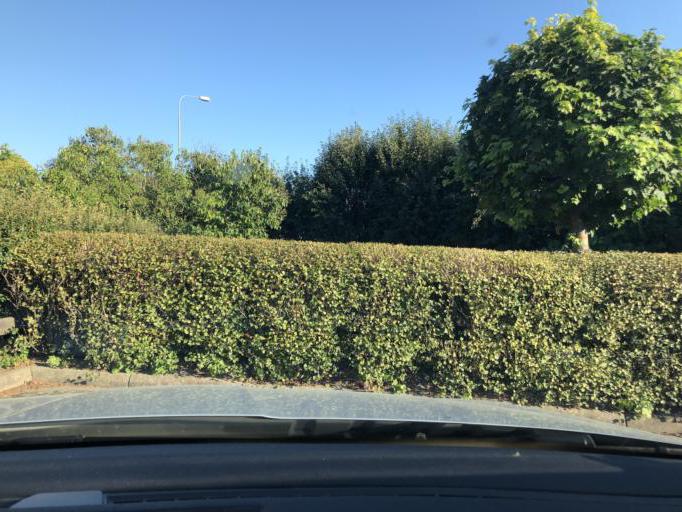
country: SE
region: Stockholm
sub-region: Sodertalje Kommun
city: Soedertaelje
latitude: 59.1828
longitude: 17.6149
